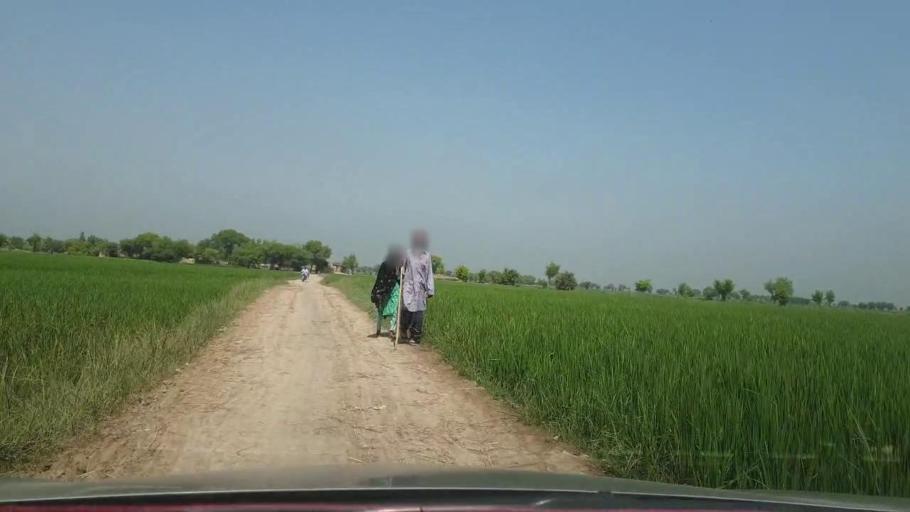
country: PK
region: Sindh
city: Kambar
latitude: 27.5930
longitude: 67.9084
